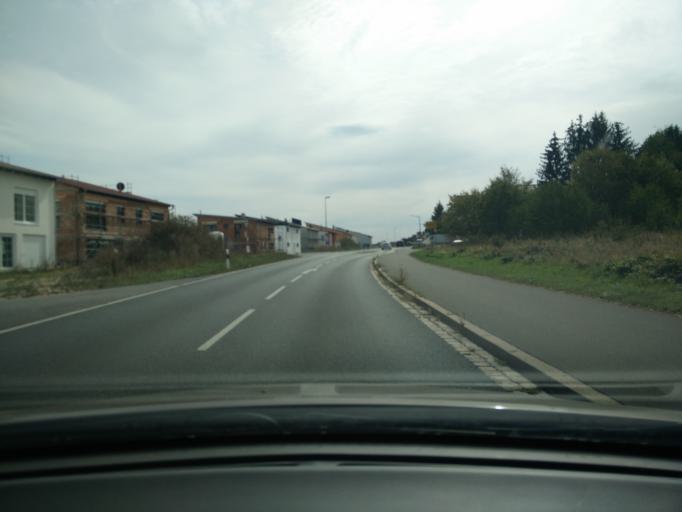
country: DE
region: Bavaria
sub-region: Regierungsbezirk Mittelfranken
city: Seukendorf
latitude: 49.4924
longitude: 10.8766
